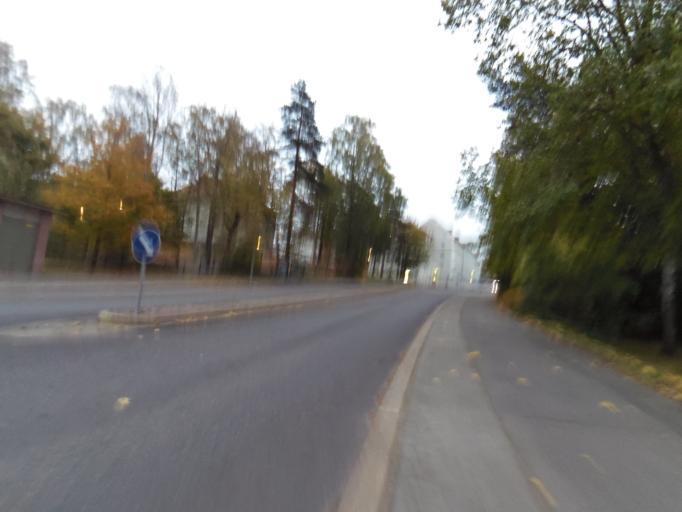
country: FI
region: Uusimaa
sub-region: Helsinki
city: Helsinki
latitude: 60.1859
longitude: 25.0001
